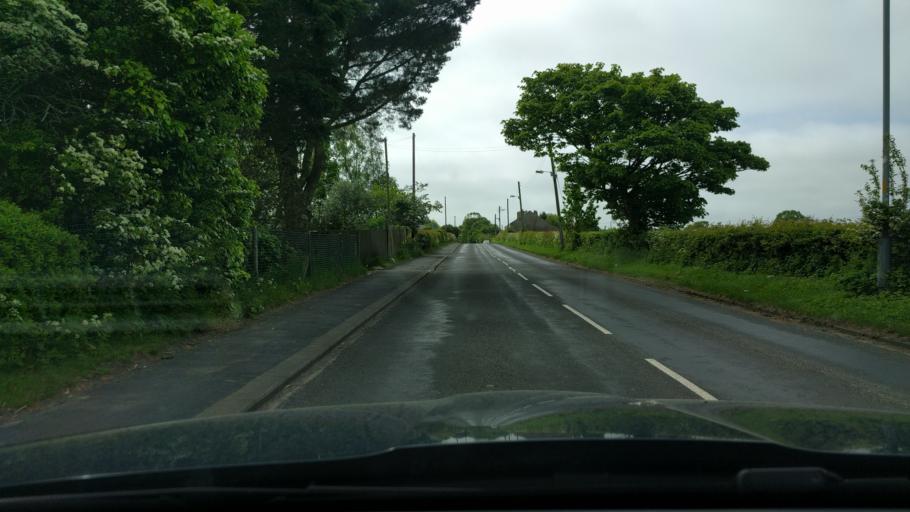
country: GB
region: England
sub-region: Northumberland
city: Acklington
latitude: 55.2999
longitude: -1.6120
